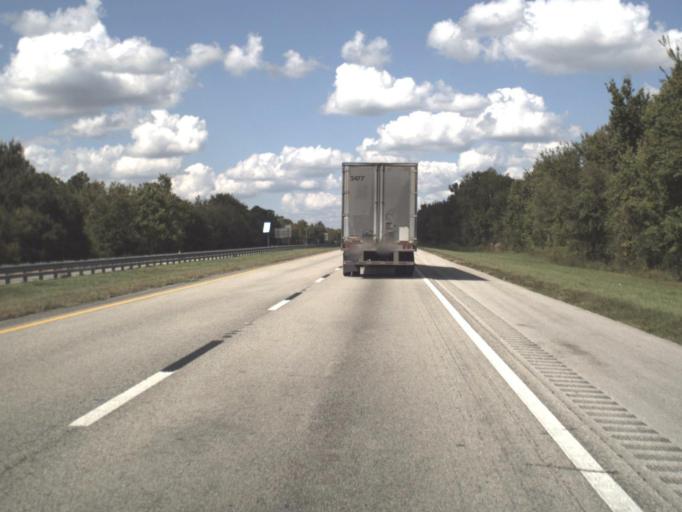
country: US
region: Florida
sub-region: Indian River County
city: Fellsmere
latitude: 27.6149
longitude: -80.8325
